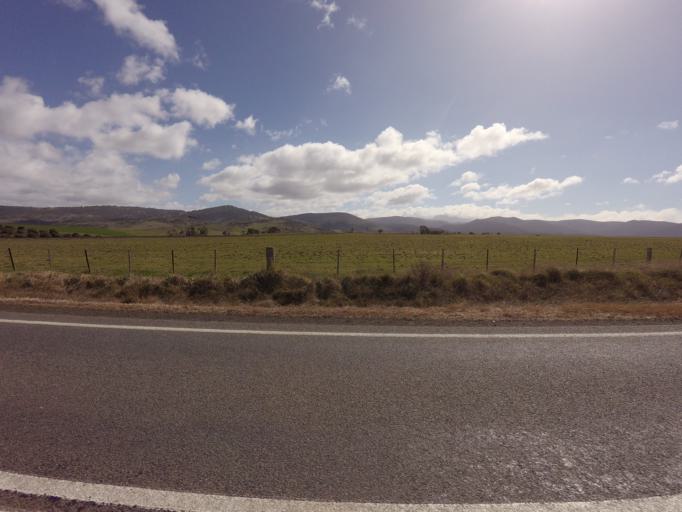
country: AU
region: Tasmania
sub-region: Northern Midlands
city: Evandale
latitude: -41.7970
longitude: 147.7056
